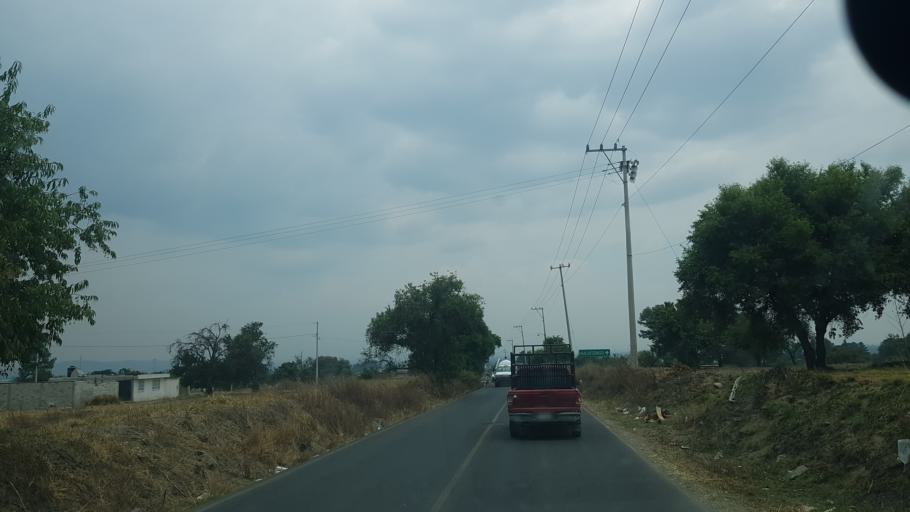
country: MX
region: Puebla
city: San Lorenzo Chiautzingo
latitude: 19.1977
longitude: -98.4488
